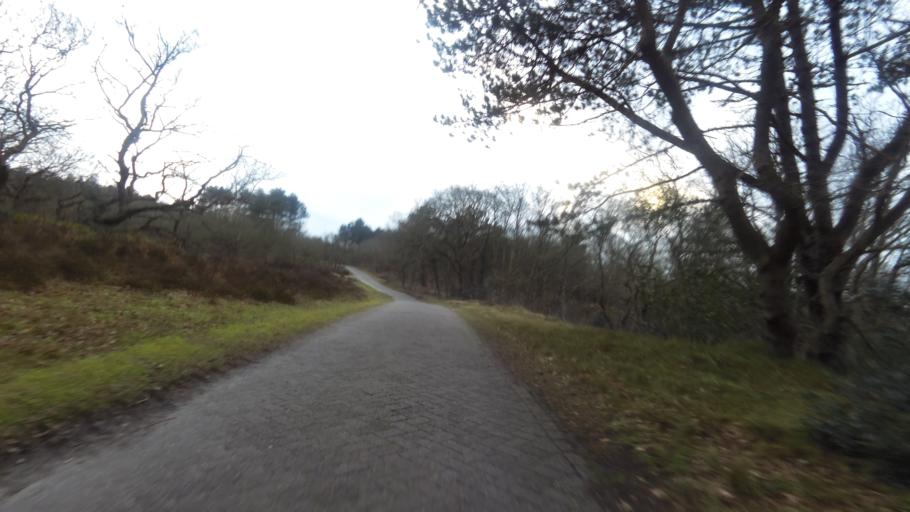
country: NL
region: North Holland
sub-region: Gemeente Heiloo
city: Heiloo
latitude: 52.6802
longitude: 4.6875
